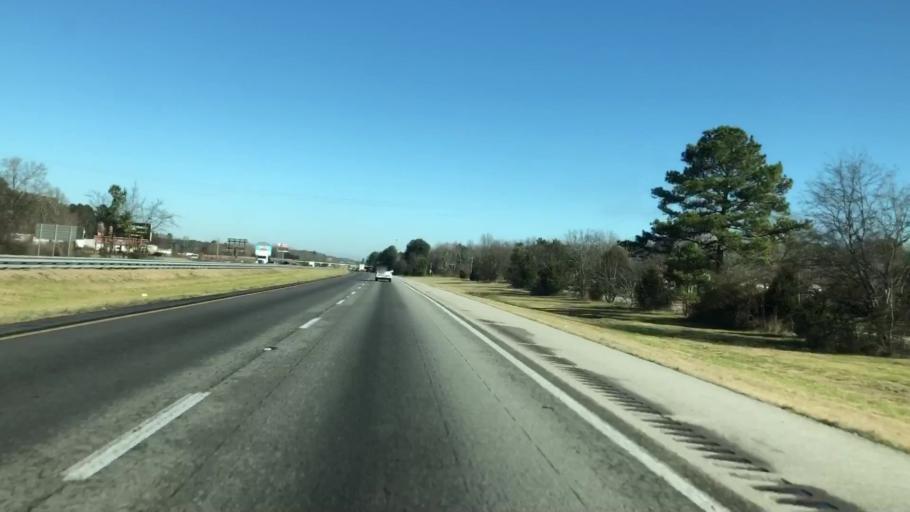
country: US
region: Alabama
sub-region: Limestone County
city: Athens
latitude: 34.8538
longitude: -86.9287
